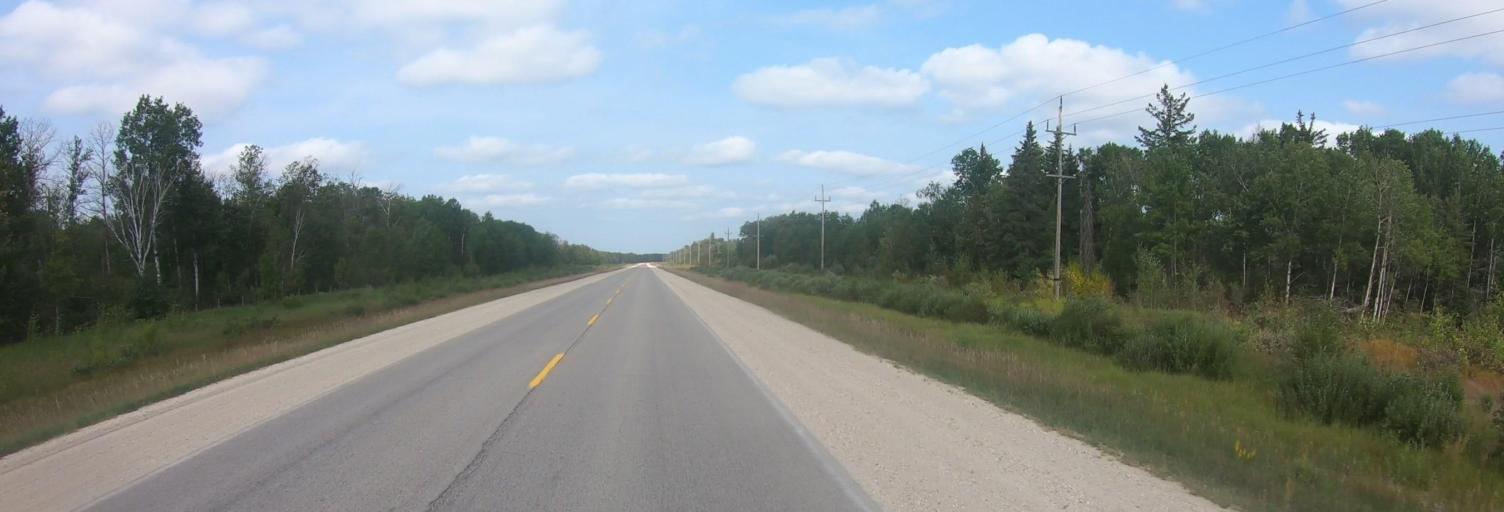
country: CA
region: Manitoba
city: La Broquerie
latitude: 49.2312
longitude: -96.3305
